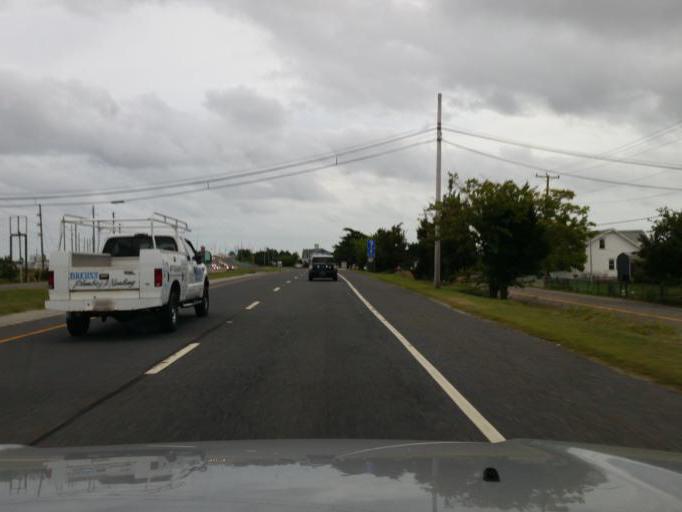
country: US
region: New Jersey
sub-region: Cape May County
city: Wildwood Crest
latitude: 38.9939
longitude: -74.8409
